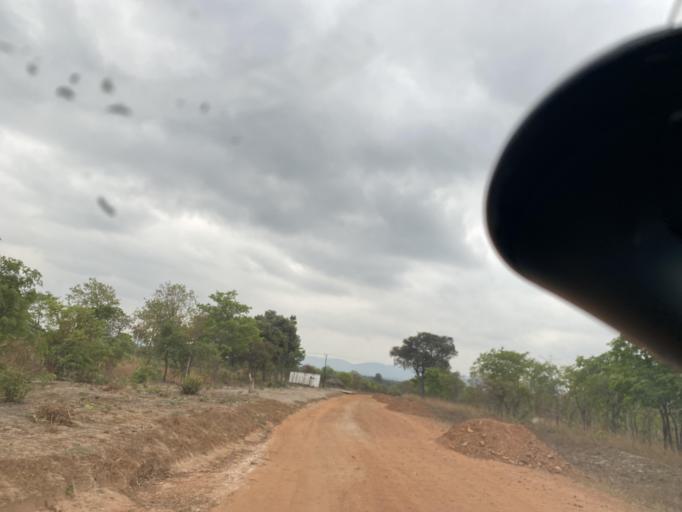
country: ZM
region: Lusaka
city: Chongwe
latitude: -15.2548
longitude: 28.7285
